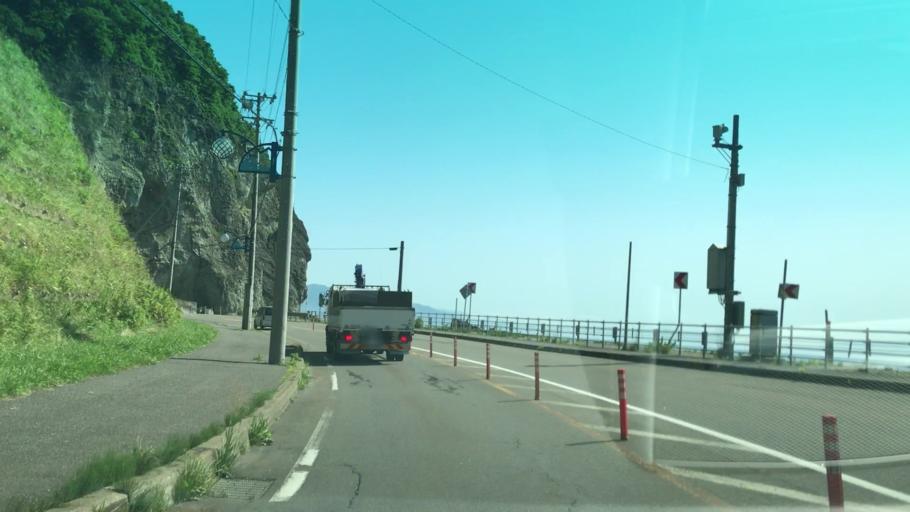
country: JP
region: Hokkaido
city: Iwanai
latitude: 43.1116
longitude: 140.4503
